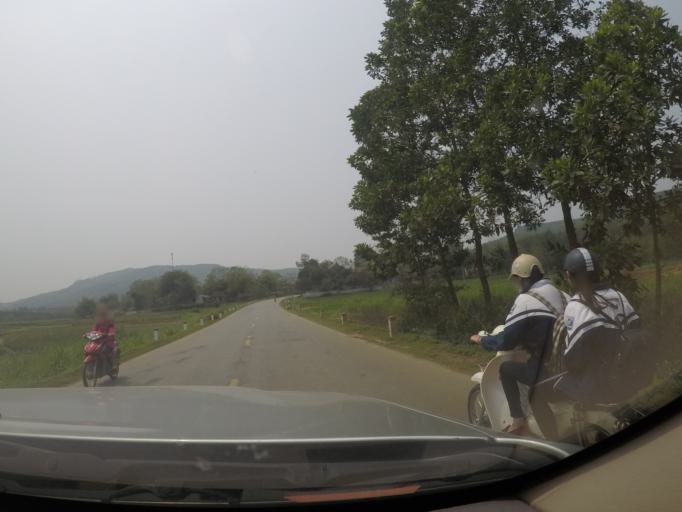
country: VN
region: Thanh Hoa
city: Thi Tran Cam Thuy
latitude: 20.1667
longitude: 105.4757
